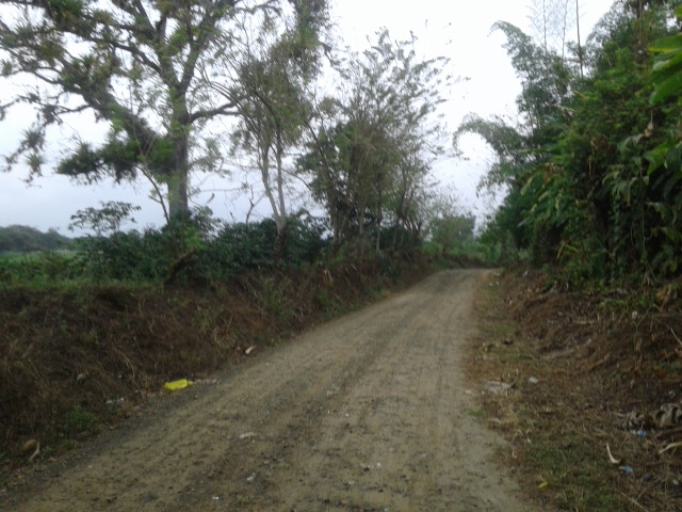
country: CO
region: Quindio
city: Quimbaya
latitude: 4.6312
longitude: -75.7728
